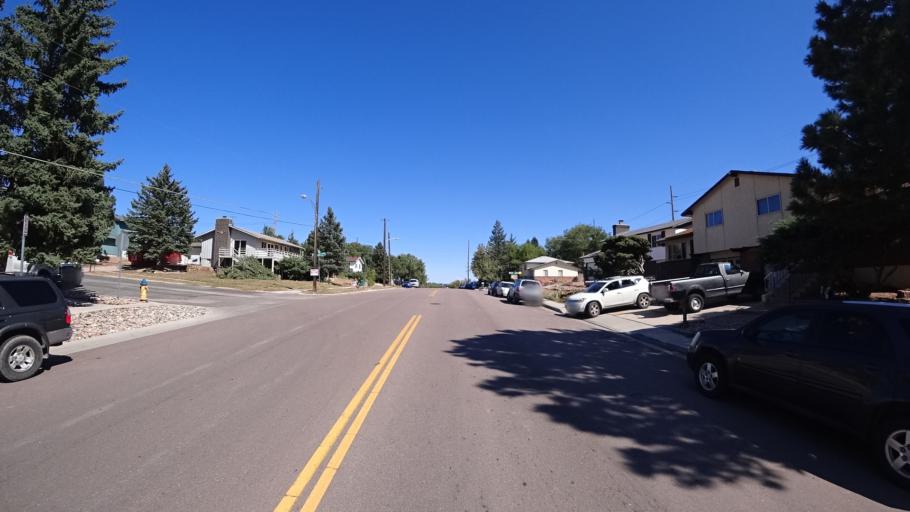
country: US
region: Colorado
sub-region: El Paso County
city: Colorado Springs
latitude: 38.8555
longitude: -104.8607
